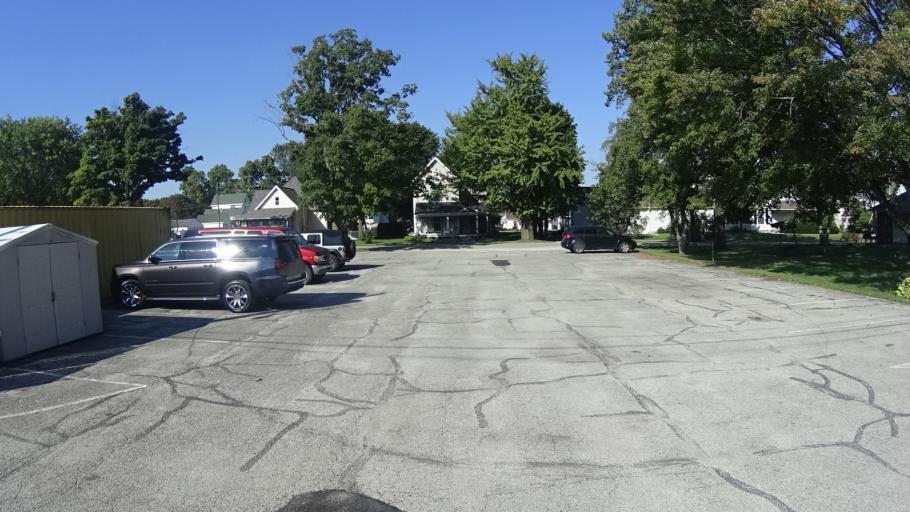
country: US
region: Indiana
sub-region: Madison County
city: Lapel
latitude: 40.0664
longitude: -85.8452
